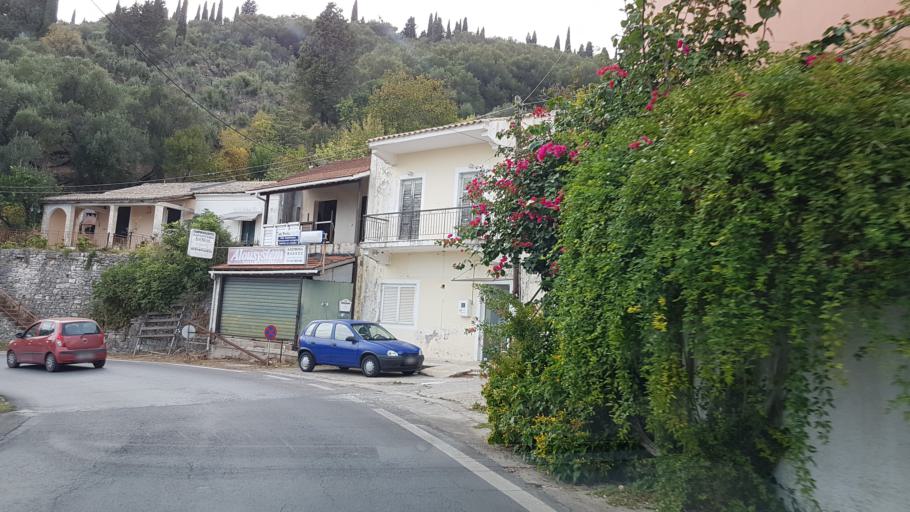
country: GR
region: Ionian Islands
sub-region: Nomos Kerkyras
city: Kerkyra
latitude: 39.7423
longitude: 19.9280
